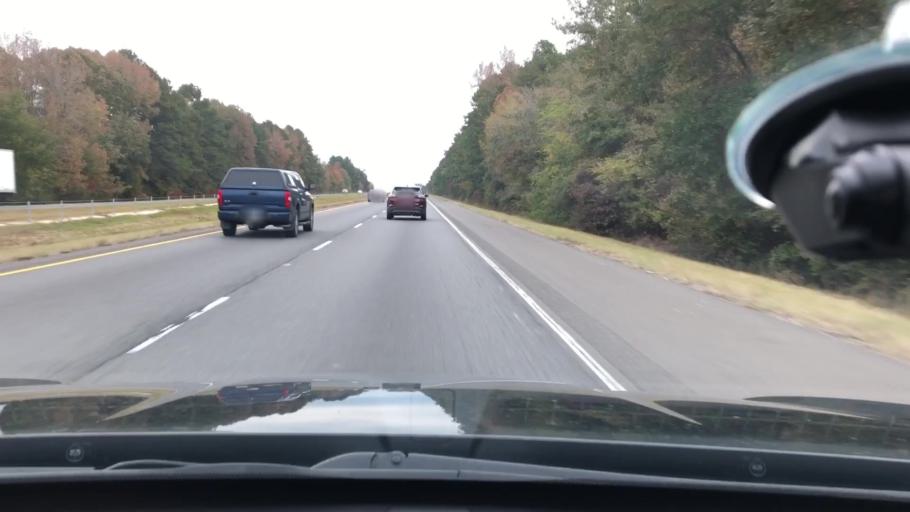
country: US
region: Arkansas
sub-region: Clark County
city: Gurdon
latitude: 34.0286
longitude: -93.1508
